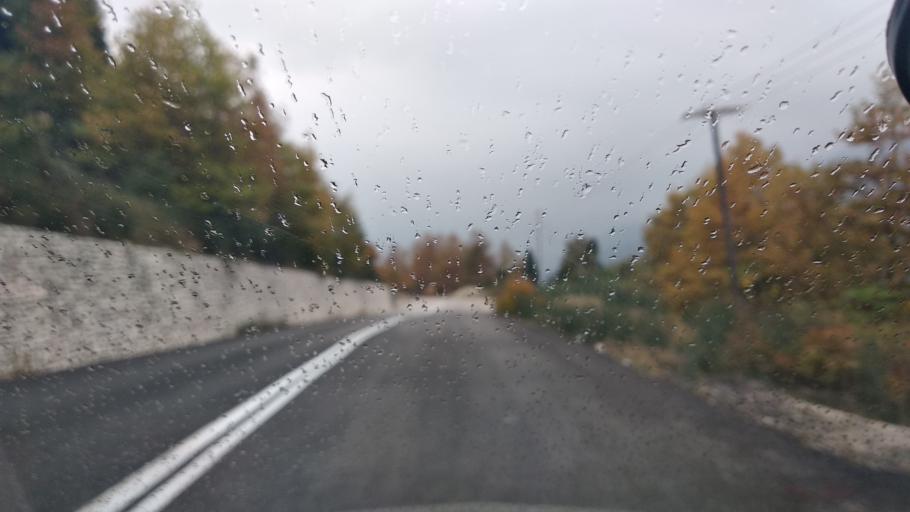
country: GR
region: Thessaly
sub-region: Trikala
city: Pyli
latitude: 39.4949
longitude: 21.5403
